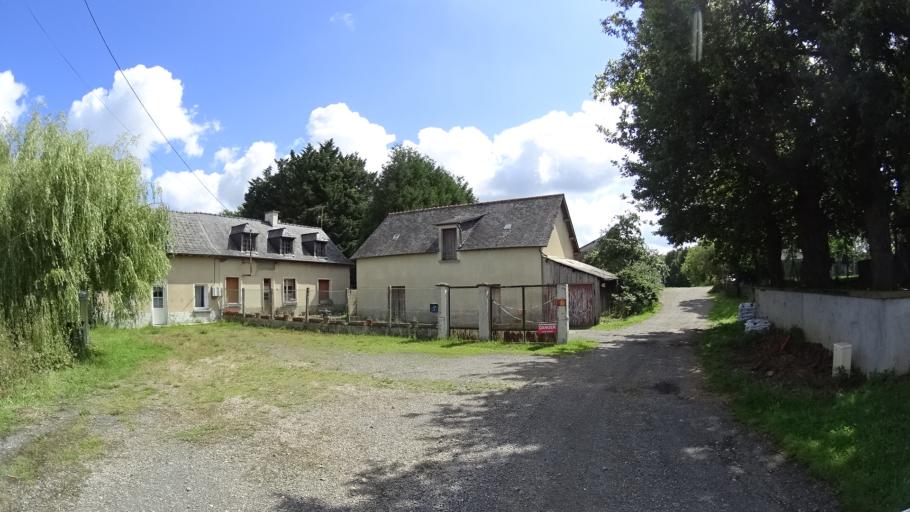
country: FR
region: Brittany
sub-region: Departement d'Ille-et-Vilaine
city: Le Rheu
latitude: 48.1158
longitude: -1.8015
